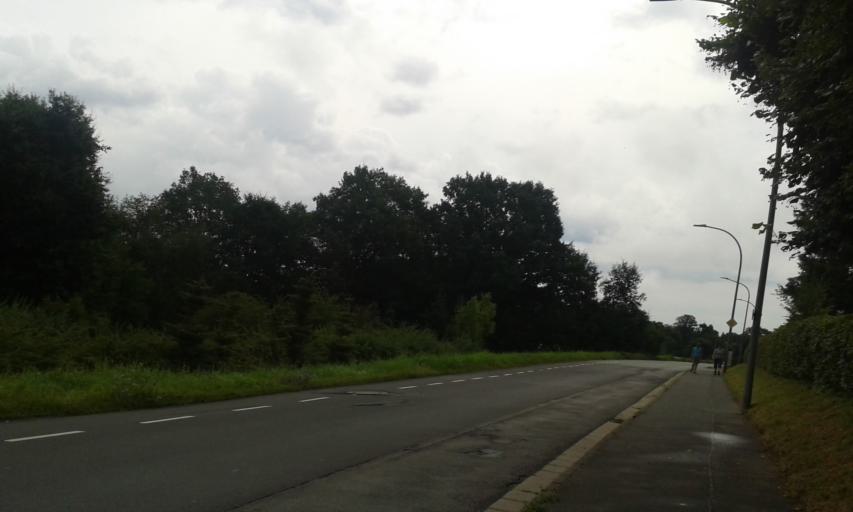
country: DE
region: Bavaria
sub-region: Upper Franconia
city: Bamberg
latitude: 49.8636
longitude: 10.9116
